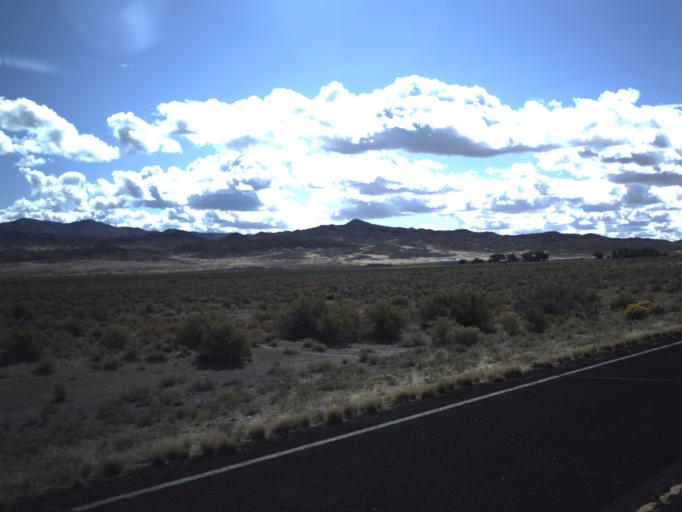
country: US
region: Nevada
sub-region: White Pine County
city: McGill
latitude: 38.9586
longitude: -114.0335
